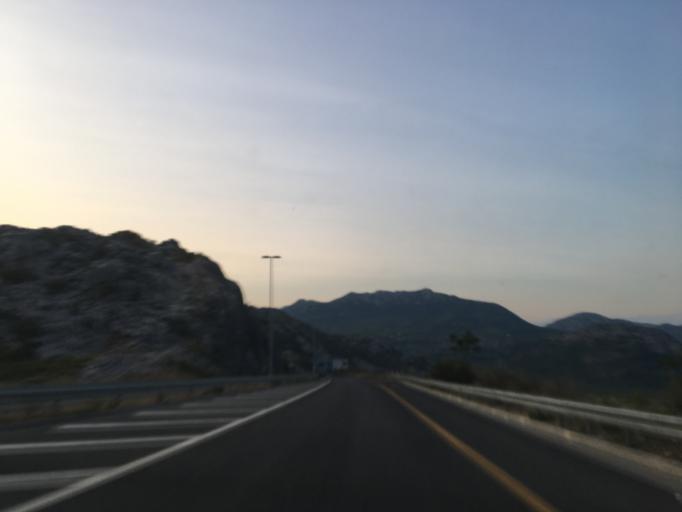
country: ME
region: Bar
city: Sutomore
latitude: 42.2036
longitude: 19.0507
